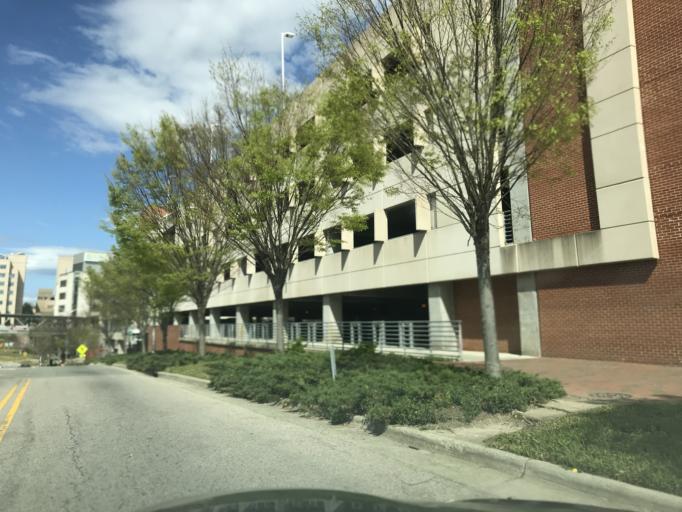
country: US
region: North Carolina
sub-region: Orange County
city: Chapel Hill
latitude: 35.9015
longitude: -79.0510
